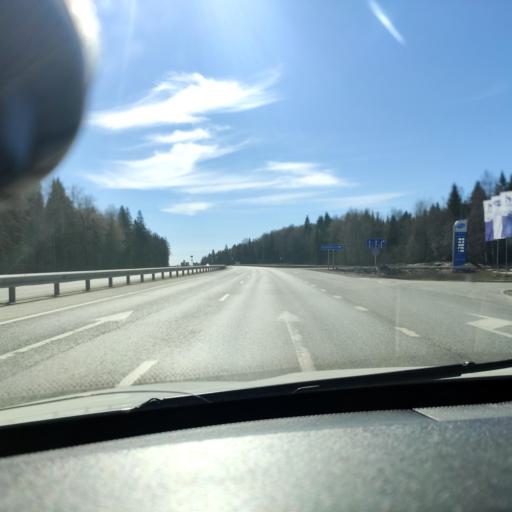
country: RU
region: Perm
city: Polazna
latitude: 58.2480
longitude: 56.4116
